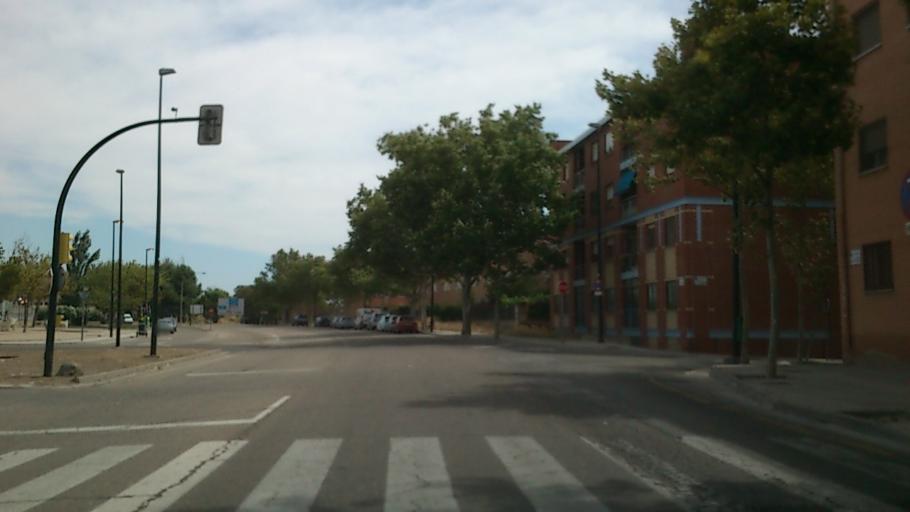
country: ES
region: Aragon
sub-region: Provincia de Zaragoza
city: Zaragoza
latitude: 41.6667
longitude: -0.8232
